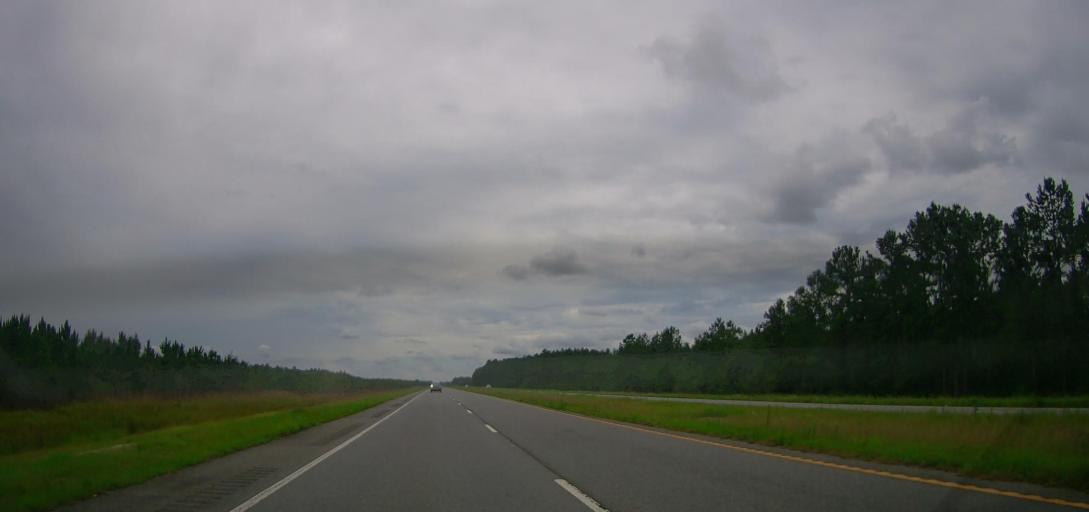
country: US
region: Georgia
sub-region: Appling County
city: Baxley
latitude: 31.7461
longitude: -82.2555
